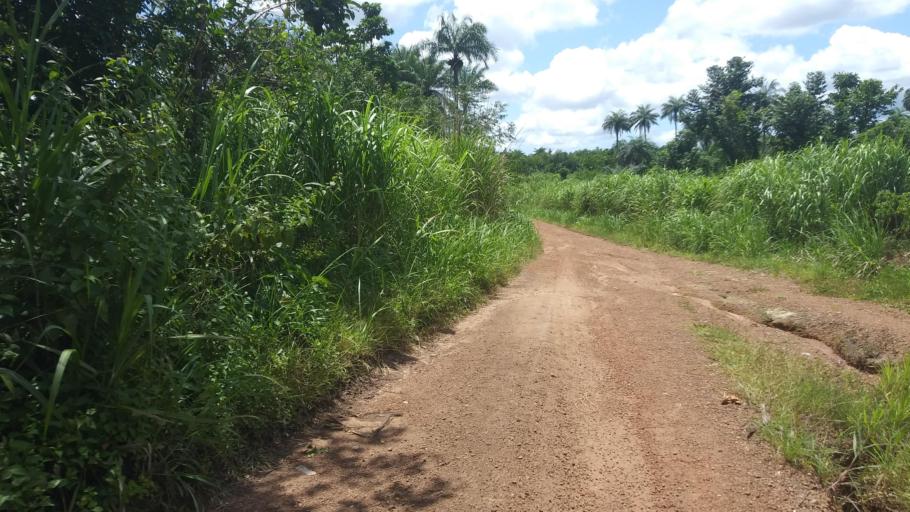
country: SL
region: Northern Province
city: Binkolo
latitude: 8.8796
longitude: -11.9636
